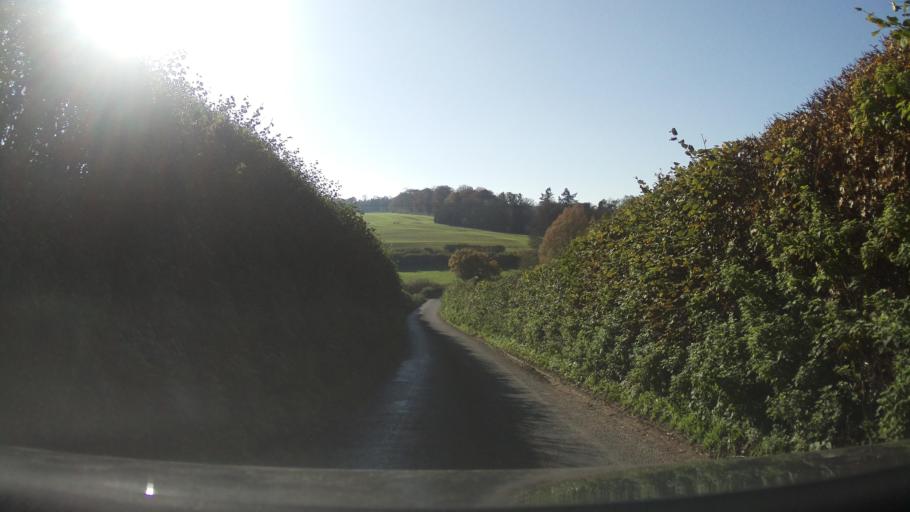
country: GB
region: England
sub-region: Somerset
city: Castle Cary
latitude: 51.0366
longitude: -2.4944
